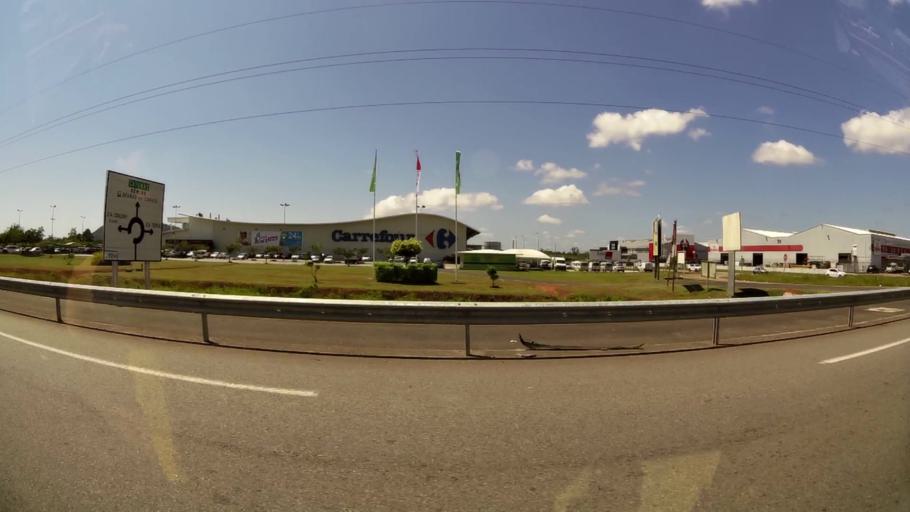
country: GF
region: Guyane
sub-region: Guyane
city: Cayenne
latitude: 4.8947
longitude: -52.3302
